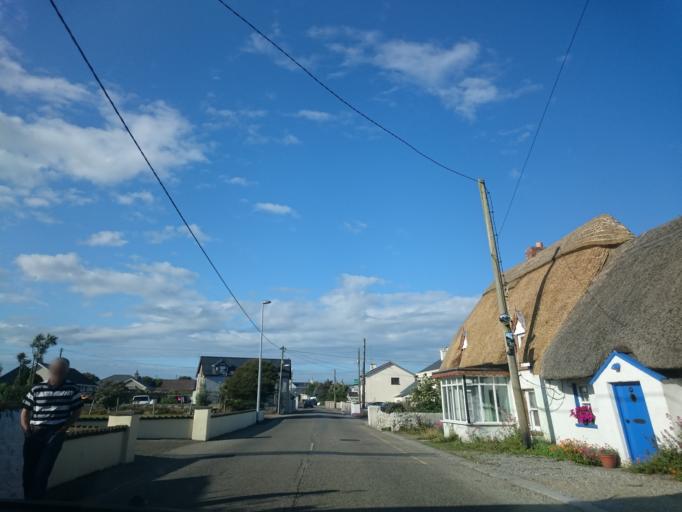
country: IE
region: Leinster
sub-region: Loch Garman
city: Loch Garman
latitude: 52.1756
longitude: -6.5863
